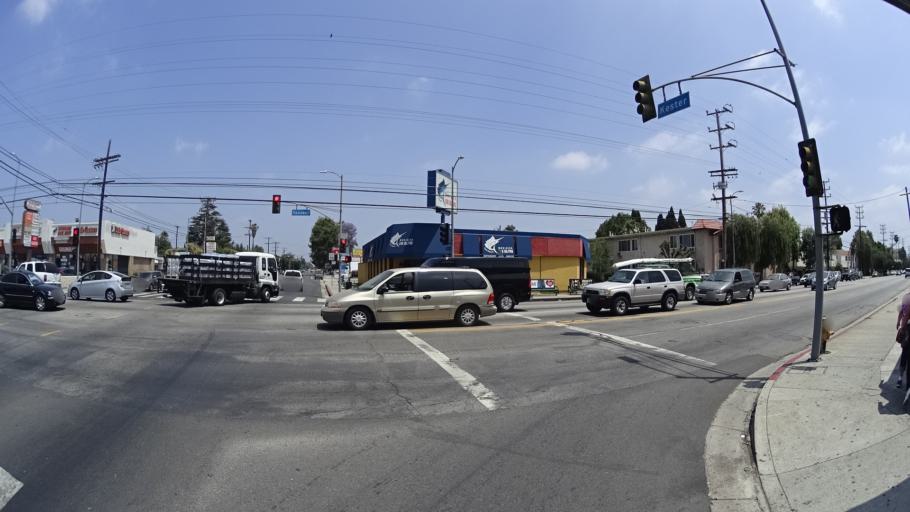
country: US
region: California
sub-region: Los Angeles County
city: Van Nuys
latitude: 34.1938
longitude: -118.4574
